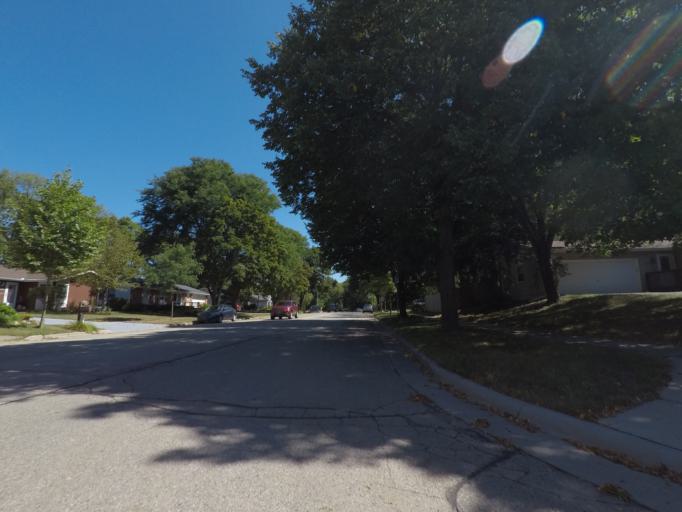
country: US
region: Wisconsin
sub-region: Dane County
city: Verona
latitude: 43.0242
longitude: -89.4996
